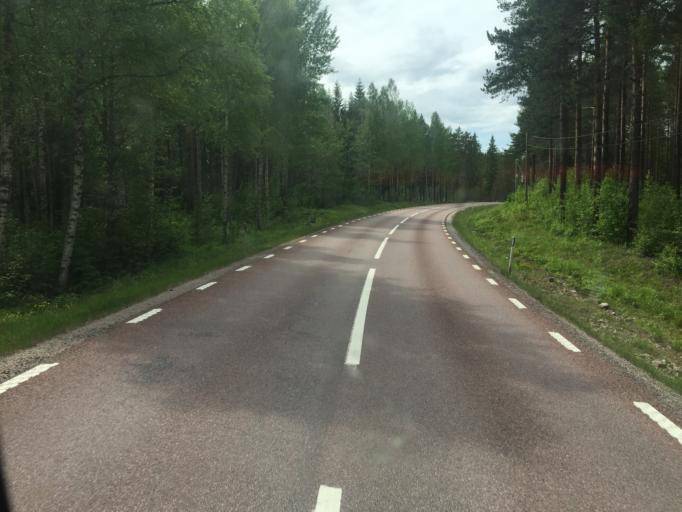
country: SE
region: Dalarna
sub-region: Vansbro Kommun
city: Vansbro
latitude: 60.4978
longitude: 14.1628
